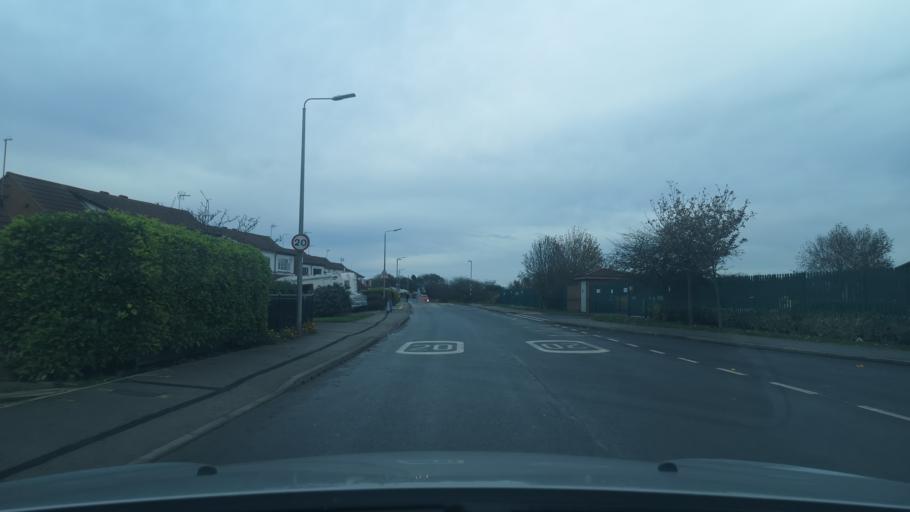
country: GB
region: England
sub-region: East Riding of Yorkshire
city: Hornsea
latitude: 53.9064
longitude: -0.1656
